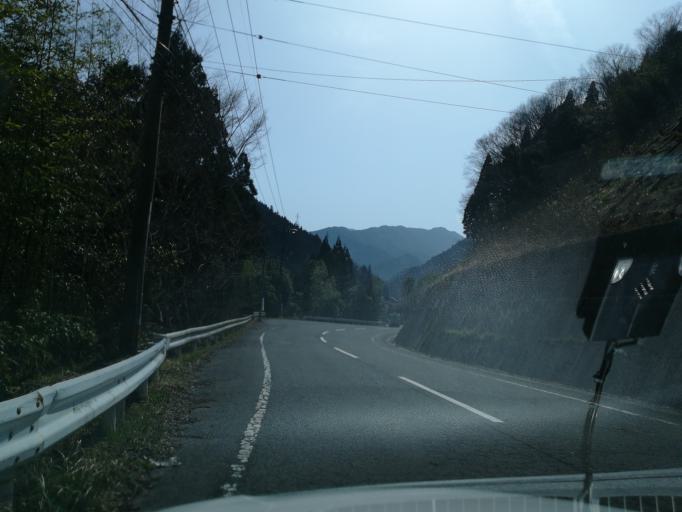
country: JP
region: Tokushima
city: Ikedacho
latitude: 33.8699
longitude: 133.9089
